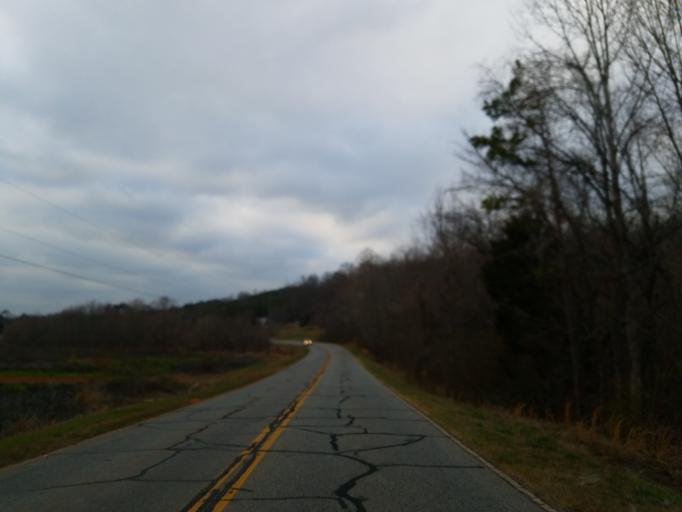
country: US
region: Georgia
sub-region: Bartow County
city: Rydal
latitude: 34.3457
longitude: -84.7085
